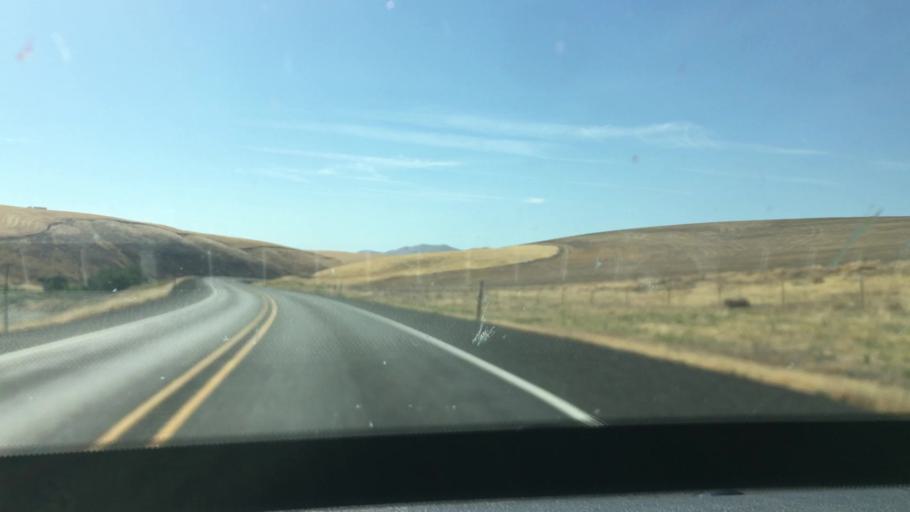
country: US
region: Oregon
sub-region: Sherman County
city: Moro
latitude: 45.6271
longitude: -120.7513
